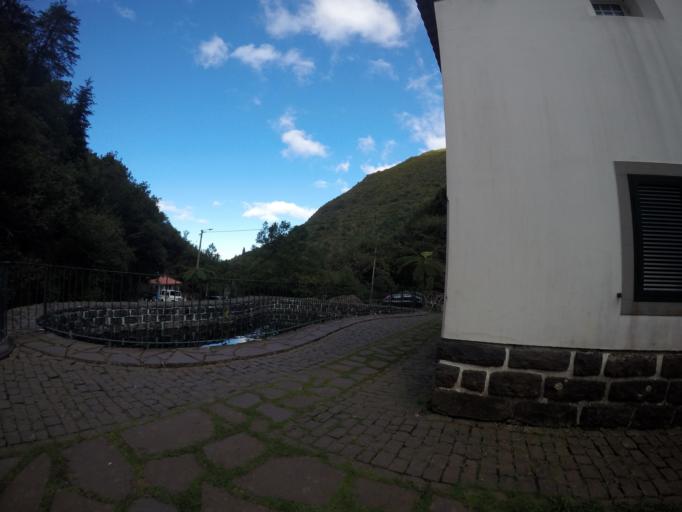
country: PT
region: Madeira
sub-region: Santana
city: Santana
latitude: 32.7343
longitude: -16.8870
